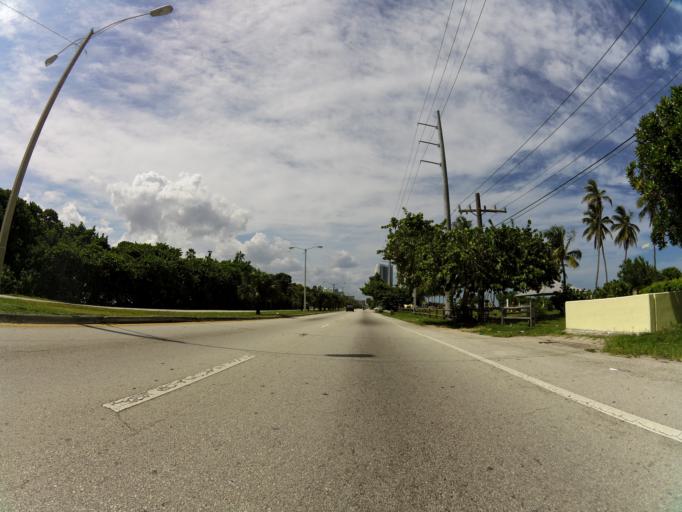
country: US
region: Florida
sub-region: Miami-Dade County
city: Bal Harbour
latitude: 25.9120
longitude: -80.1226
